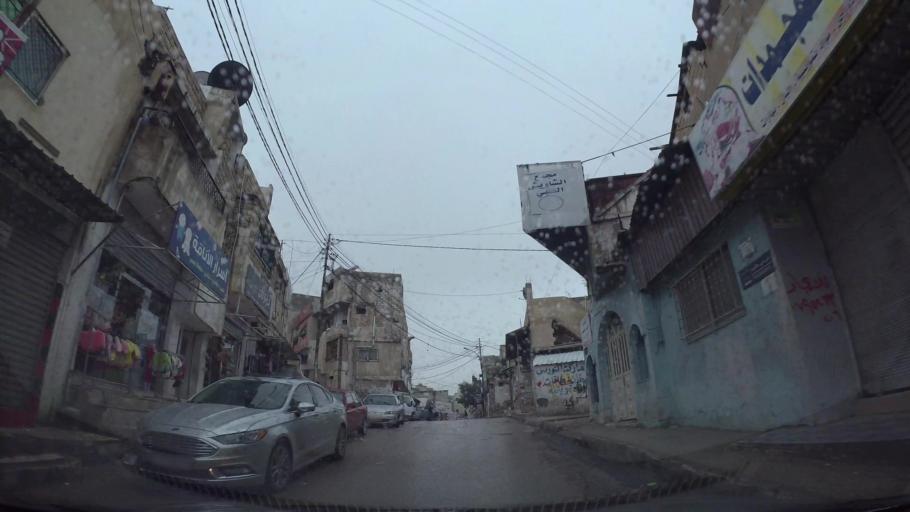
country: JO
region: Amman
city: Amman
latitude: 31.9698
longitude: 35.9256
